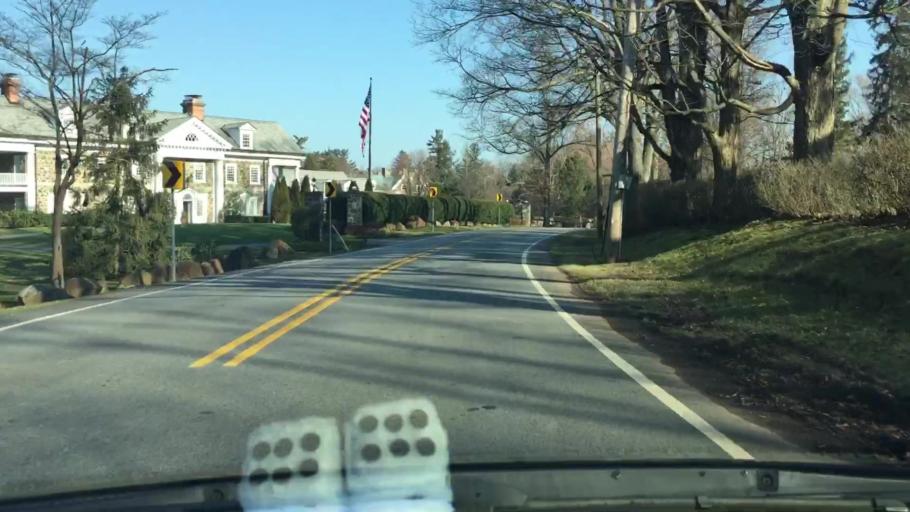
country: US
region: Pennsylvania
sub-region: Chester County
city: Devon
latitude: 40.0334
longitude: -75.4192
